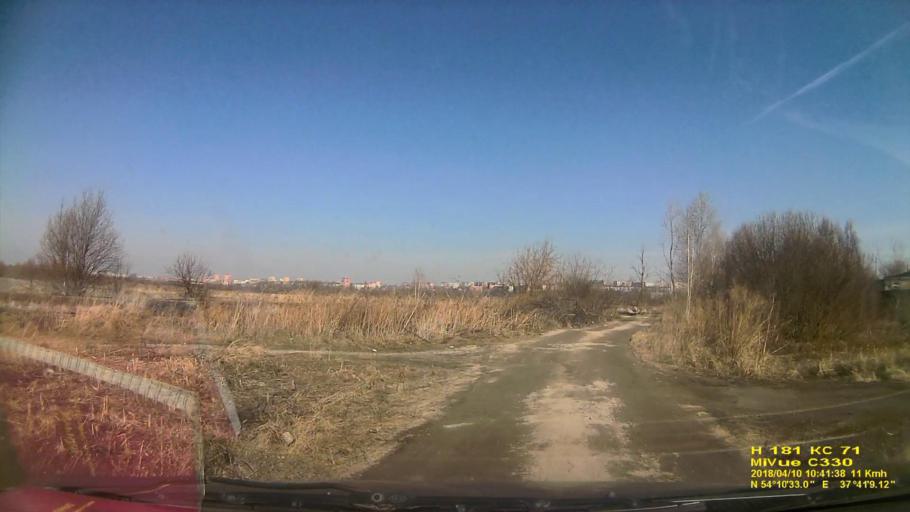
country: RU
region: Tula
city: Tula
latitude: 54.1759
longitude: 37.6858
